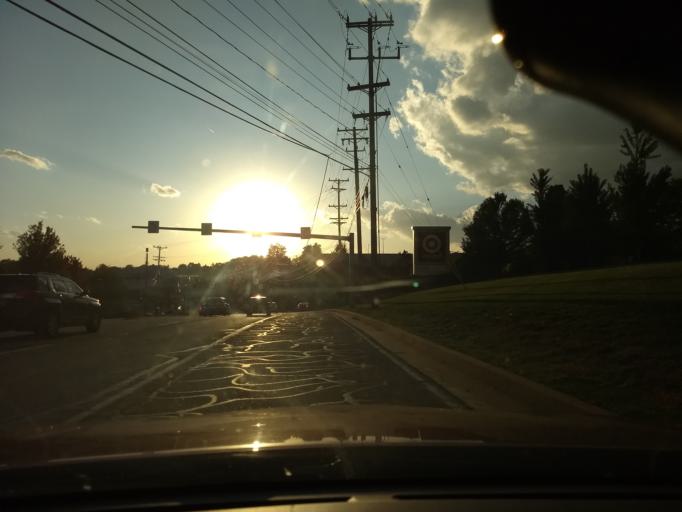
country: US
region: Pennsylvania
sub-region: Allegheny County
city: Pleasant Hills
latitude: 40.3480
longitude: -79.9504
